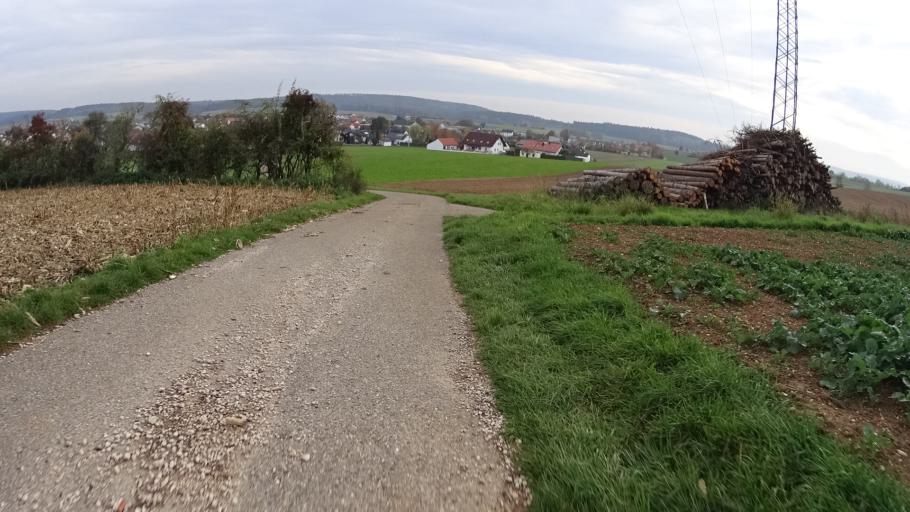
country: DE
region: Bavaria
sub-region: Upper Bavaria
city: Adelschlag
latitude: 48.8670
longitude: 11.2343
